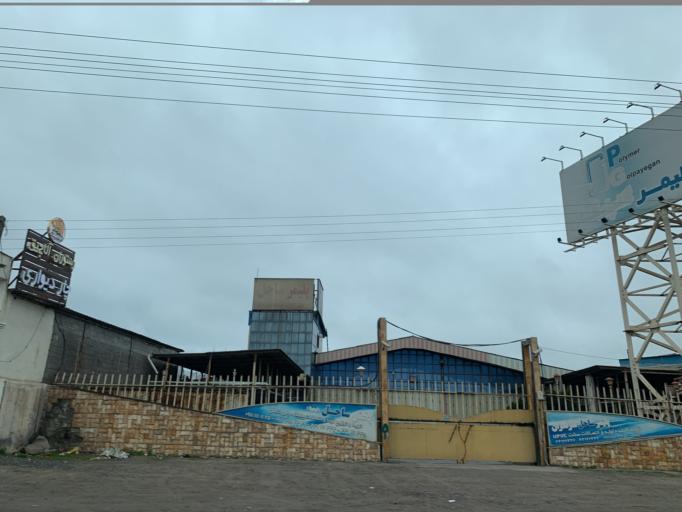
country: IR
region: Mazandaran
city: Amol
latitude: 36.4134
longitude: 52.3483
